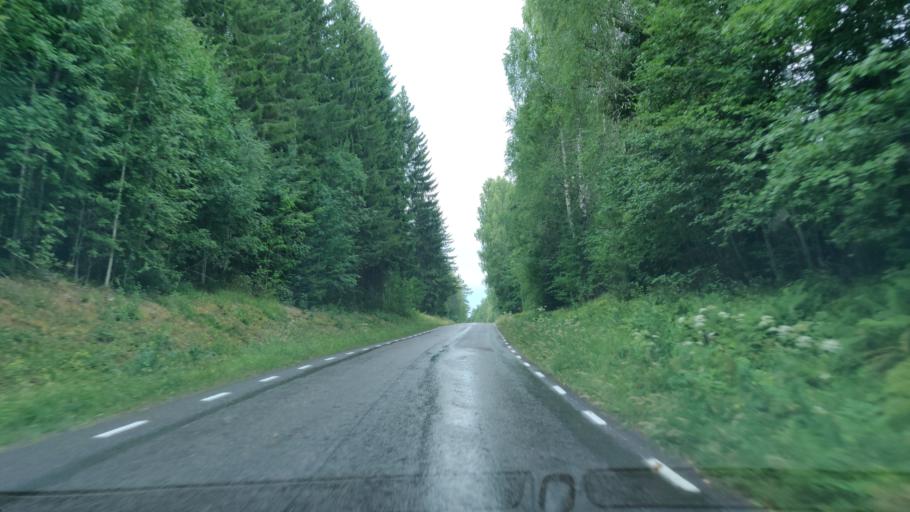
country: SE
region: Vaermland
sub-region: Munkfors Kommun
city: Munkfors
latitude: 59.8762
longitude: 13.5228
